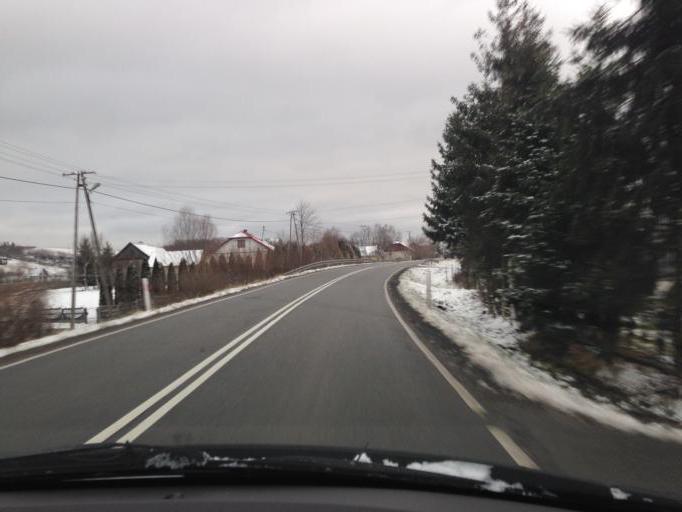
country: PL
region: Lesser Poland Voivodeship
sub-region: Powiat tarnowski
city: Siemiechow
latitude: 49.8509
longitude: 20.9197
